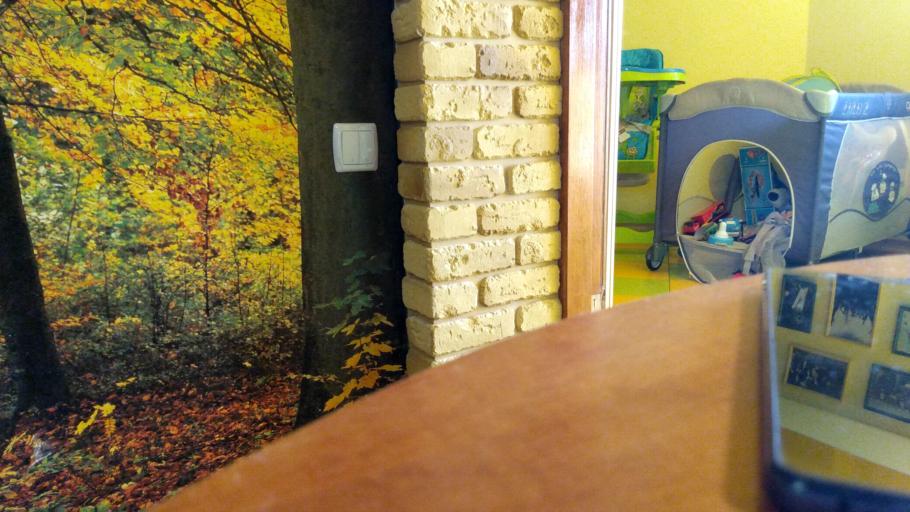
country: RU
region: Tverskaya
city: Kalashnikovo
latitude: 57.3627
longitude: 35.2250
